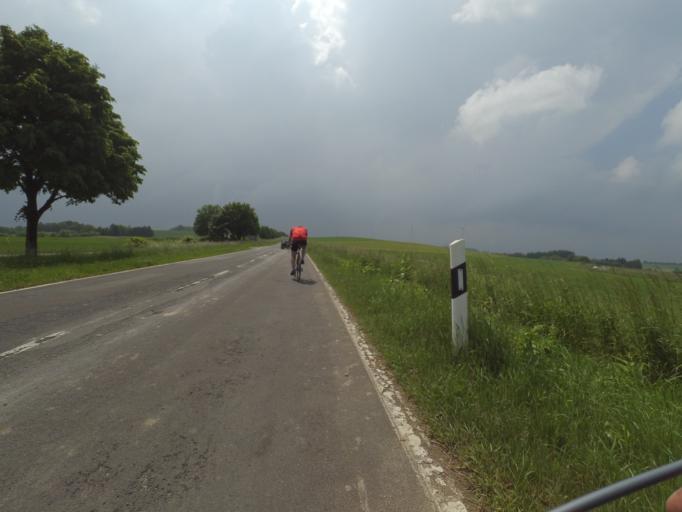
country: DE
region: Rheinland-Pfalz
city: Mastershausen
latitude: 50.0600
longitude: 7.3476
